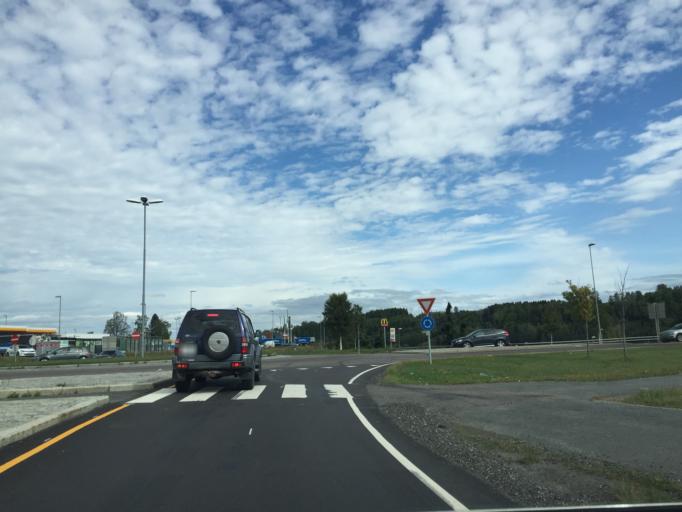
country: NO
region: Akershus
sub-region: Ski
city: Ski
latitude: 59.7238
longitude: 10.7836
